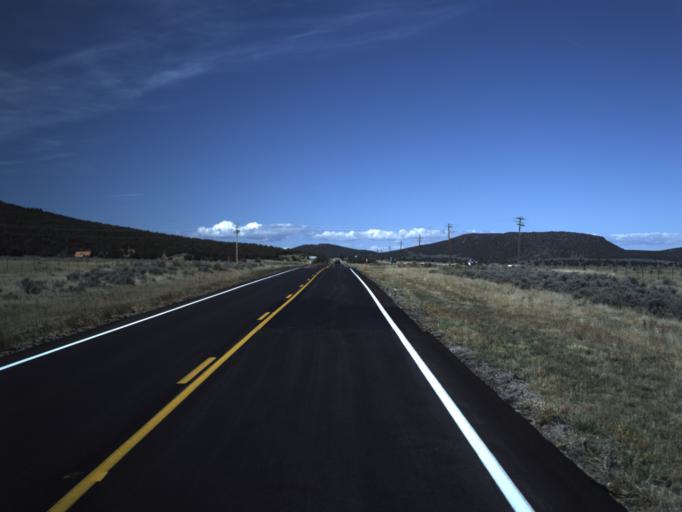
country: US
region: Utah
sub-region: Washington County
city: Enterprise
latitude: 37.4977
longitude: -113.6312
